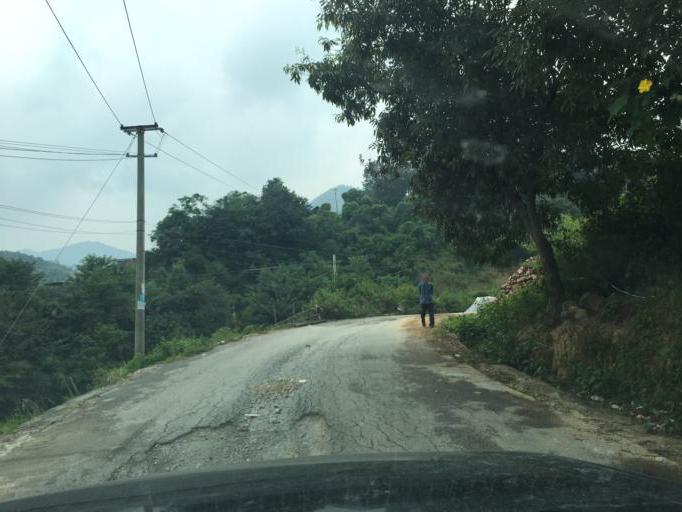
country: CN
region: Guangxi Zhuangzu Zizhiqu
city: Tongle
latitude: 25.1113
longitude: 106.2710
